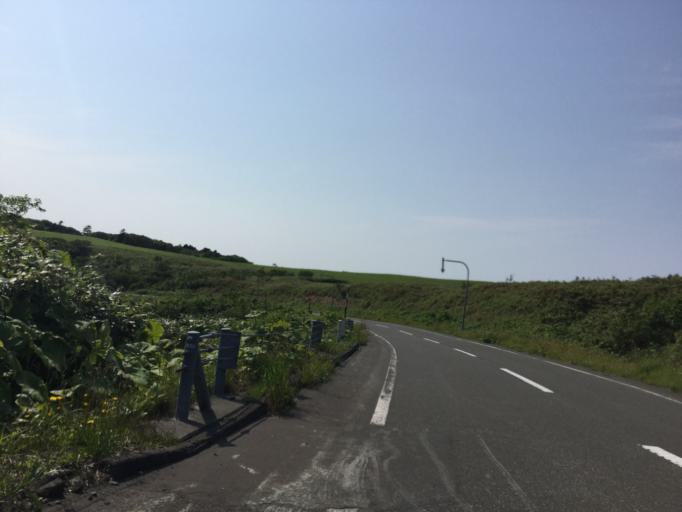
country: JP
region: Hokkaido
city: Makubetsu
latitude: 45.4985
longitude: 141.9112
